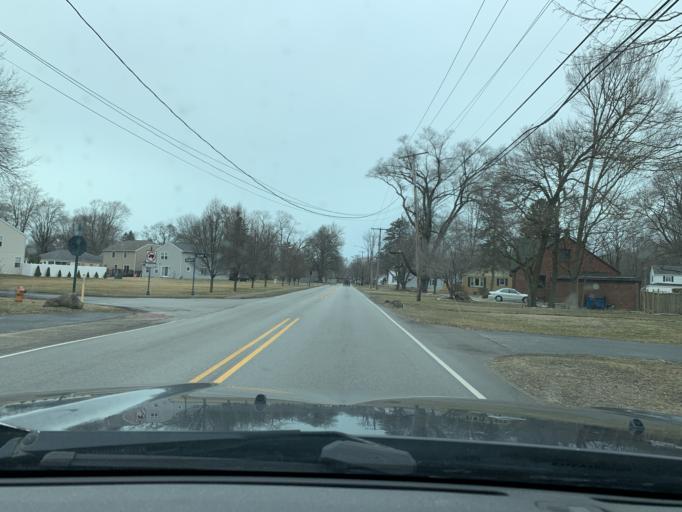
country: US
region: Indiana
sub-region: Porter County
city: Chesterton
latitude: 41.6016
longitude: -87.0498
